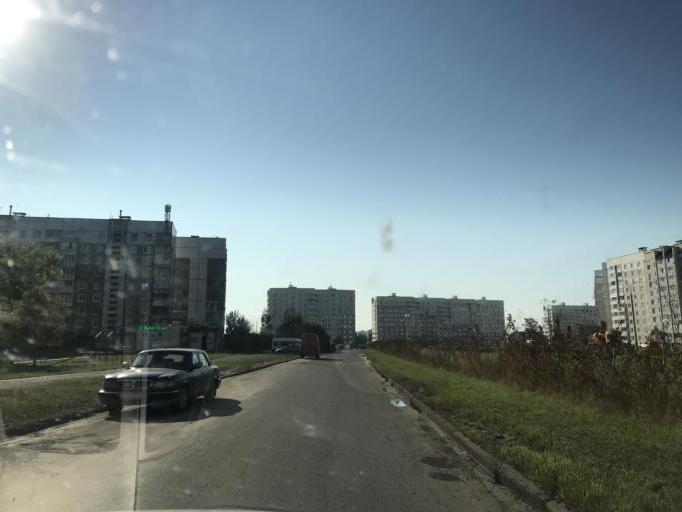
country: BY
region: Mogilev
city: Mahilyow
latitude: 53.8790
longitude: 30.3630
